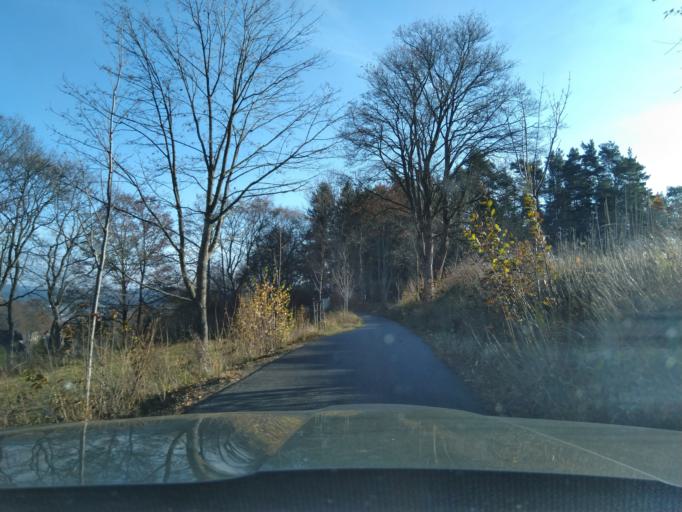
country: CZ
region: Jihocesky
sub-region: Okres Prachatice
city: Vimperk
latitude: 49.0589
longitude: 13.7650
